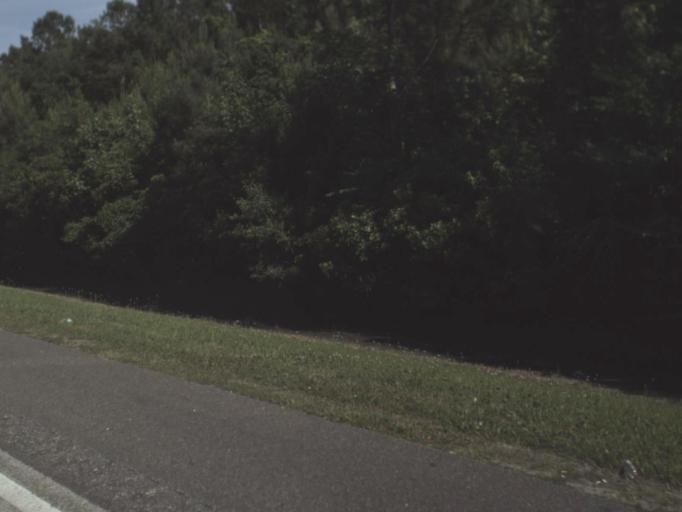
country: US
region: Florida
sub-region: Duval County
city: Jacksonville
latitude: 30.2499
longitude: -81.5656
